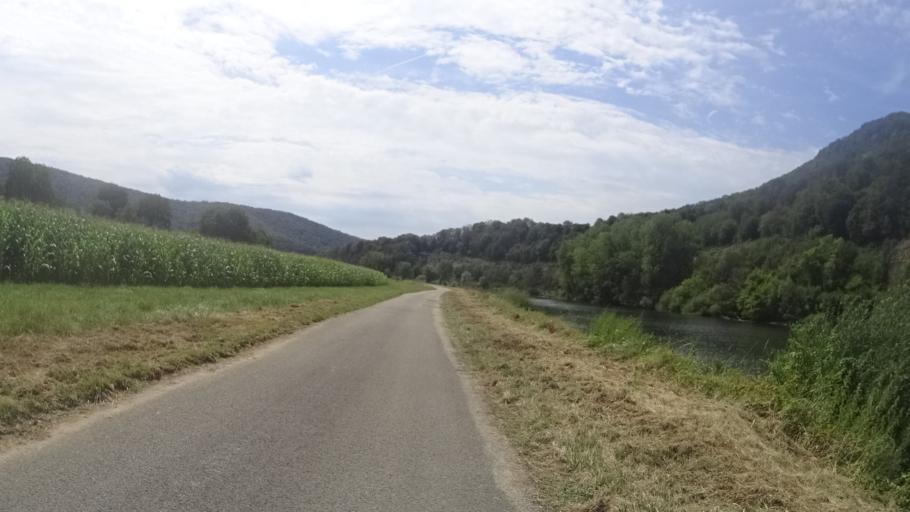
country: FR
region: Franche-Comte
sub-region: Departement du Doubs
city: Clerval
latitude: 47.3730
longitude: 6.4569
